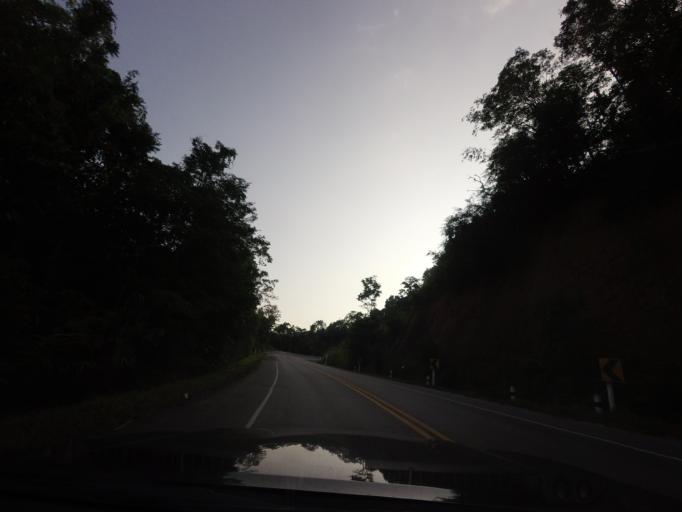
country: TH
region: Loei
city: Dan Sai
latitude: 17.3135
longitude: 101.1242
